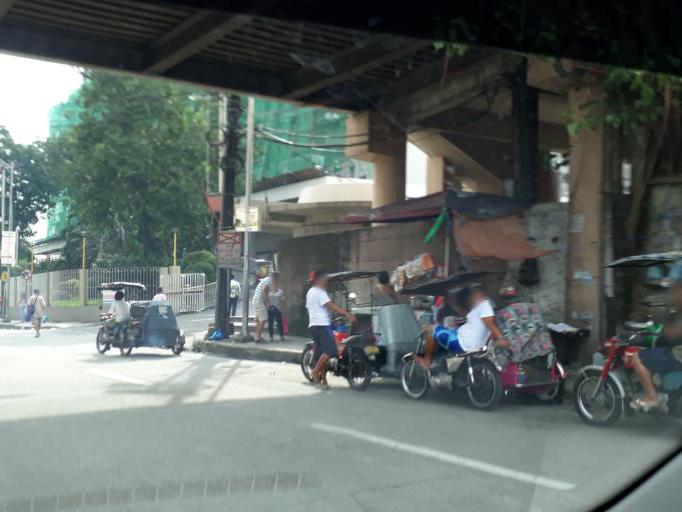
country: PH
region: Metro Manila
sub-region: City of Manila
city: Manila
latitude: 14.6258
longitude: 120.9889
